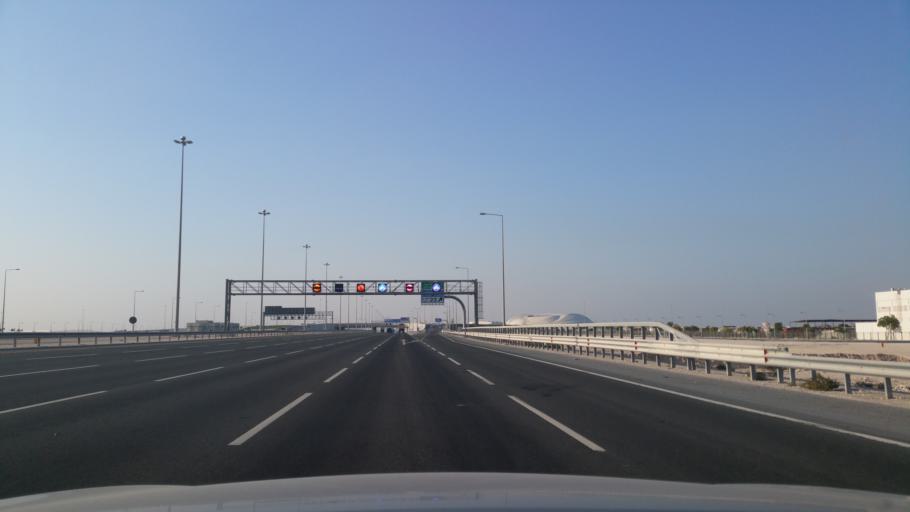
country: QA
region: Al Wakrah
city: Al Wakrah
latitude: 25.1475
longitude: 51.5763
